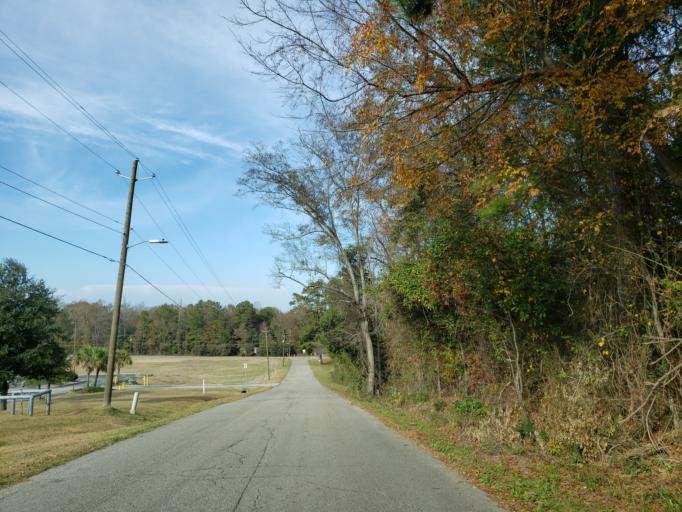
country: US
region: Mississippi
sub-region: Forrest County
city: Glendale
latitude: 31.3526
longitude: -89.3352
